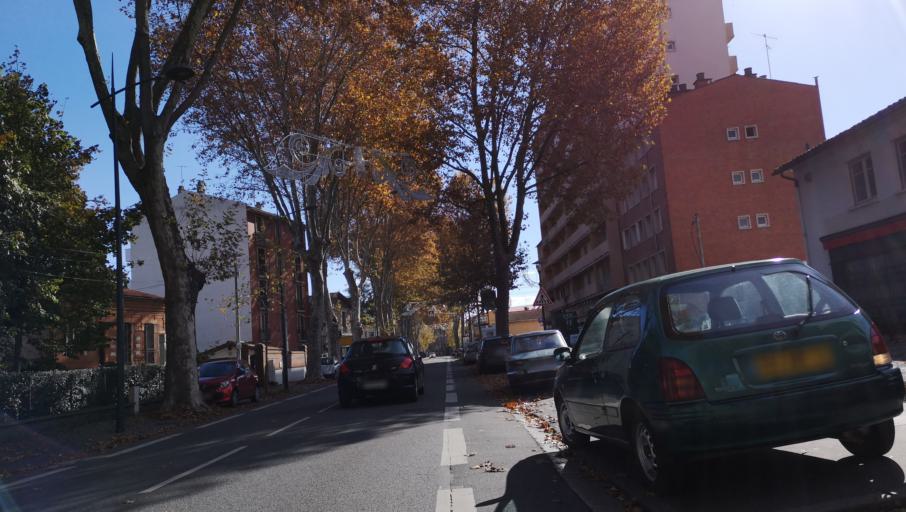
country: FR
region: Midi-Pyrenees
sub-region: Departement de la Haute-Garonne
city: Blagnac
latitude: 43.6139
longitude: 1.4116
